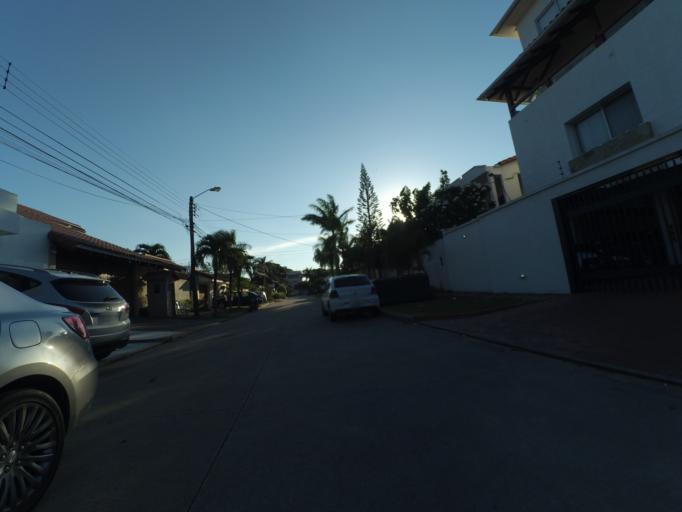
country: BO
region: Santa Cruz
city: Santa Cruz de la Sierra
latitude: -17.8061
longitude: -63.2077
